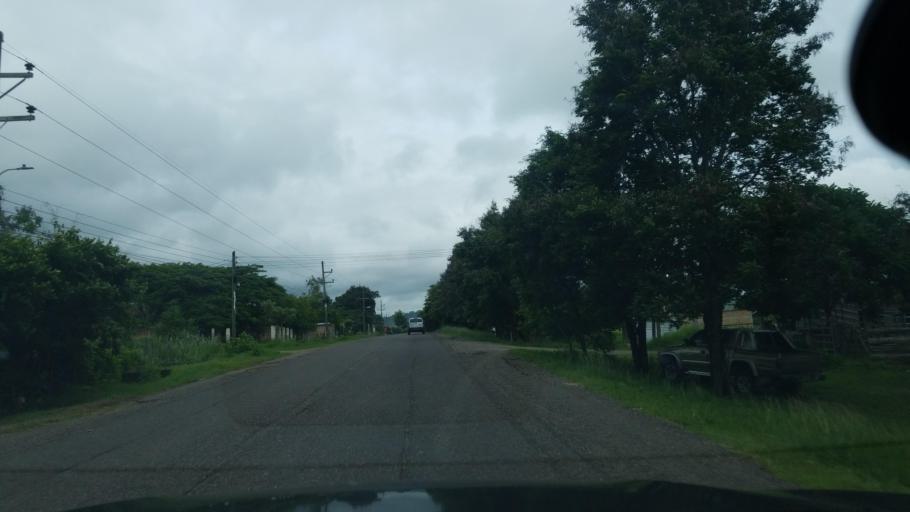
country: HN
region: Choluteca
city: San Marcos de Colon
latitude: 13.4144
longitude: -86.8390
